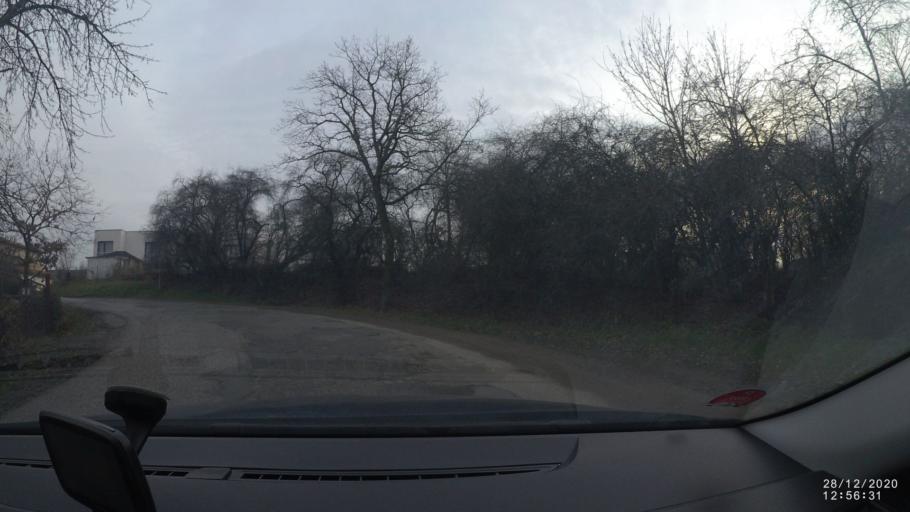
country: CZ
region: Praha
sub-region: Praha 19
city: Satalice
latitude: 50.1532
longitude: 14.5846
